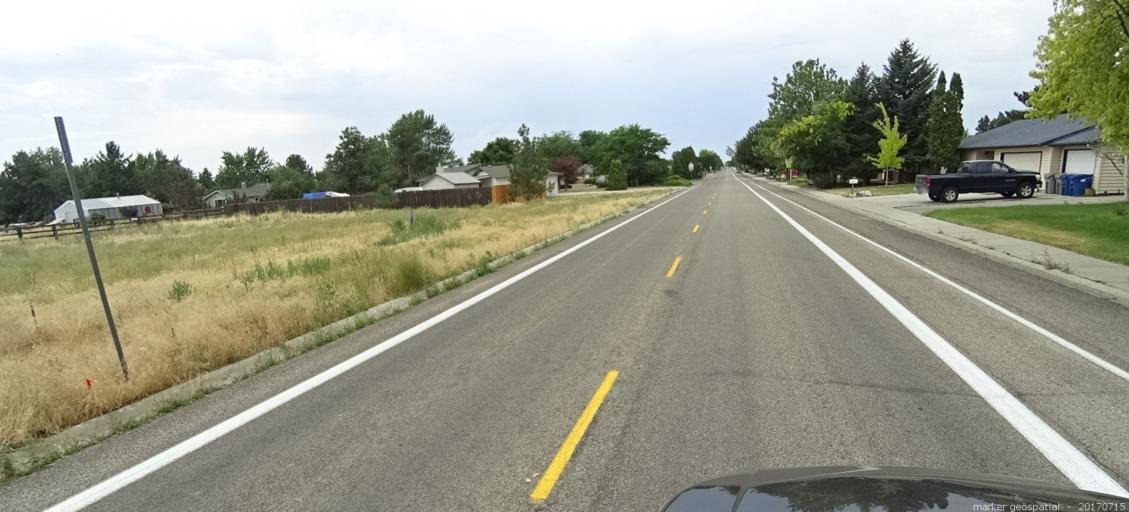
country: US
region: Idaho
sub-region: Ada County
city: Garden City
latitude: 43.5540
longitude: -116.2803
